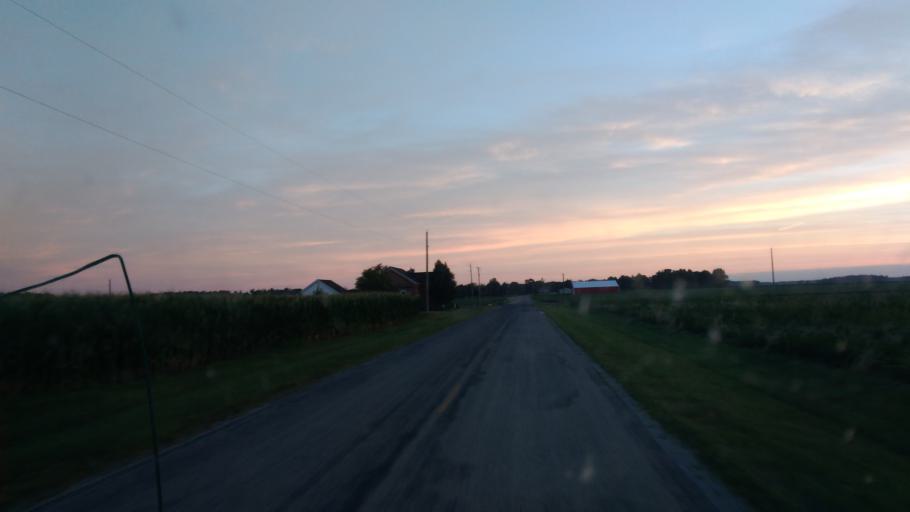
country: US
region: Indiana
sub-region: Wells County
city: Bluffton
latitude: 40.6612
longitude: -85.1263
